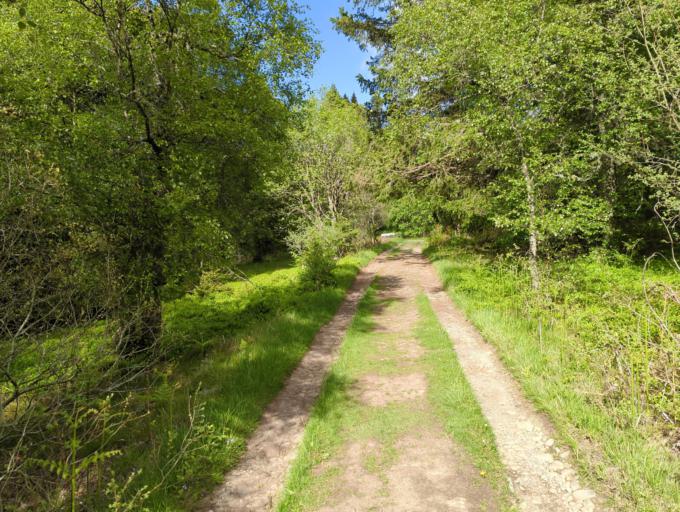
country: GB
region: Scotland
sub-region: Perth and Kinross
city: Bankfoot
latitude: 56.5529
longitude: -3.6147
